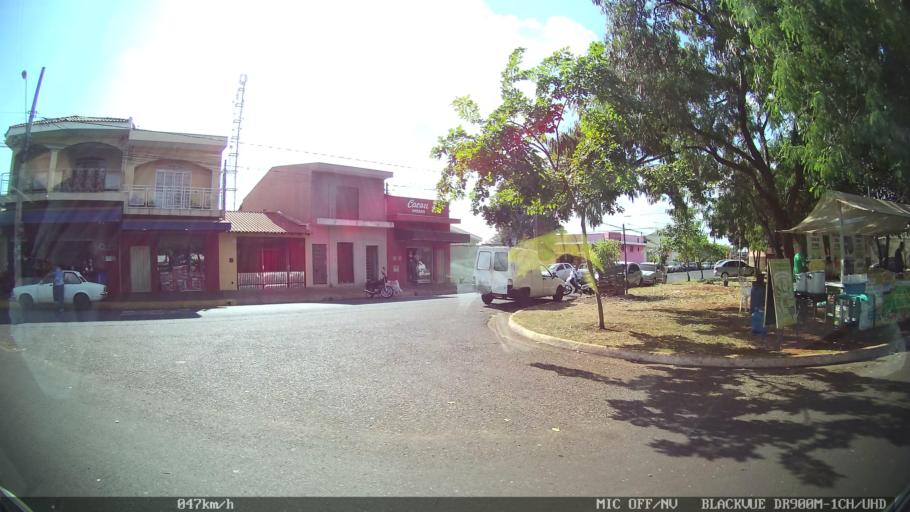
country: BR
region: Sao Paulo
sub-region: Ribeirao Preto
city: Ribeirao Preto
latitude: -21.2028
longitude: -47.8452
